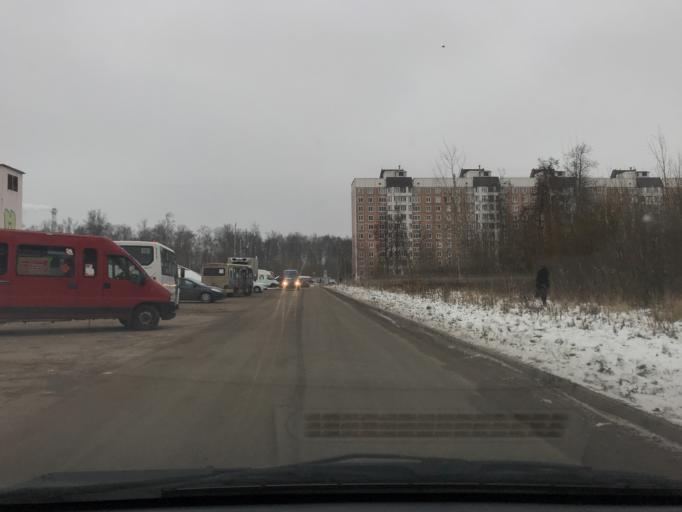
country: RU
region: Moskovskaya
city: Elektrostal'
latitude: 55.8117
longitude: 38.4305
